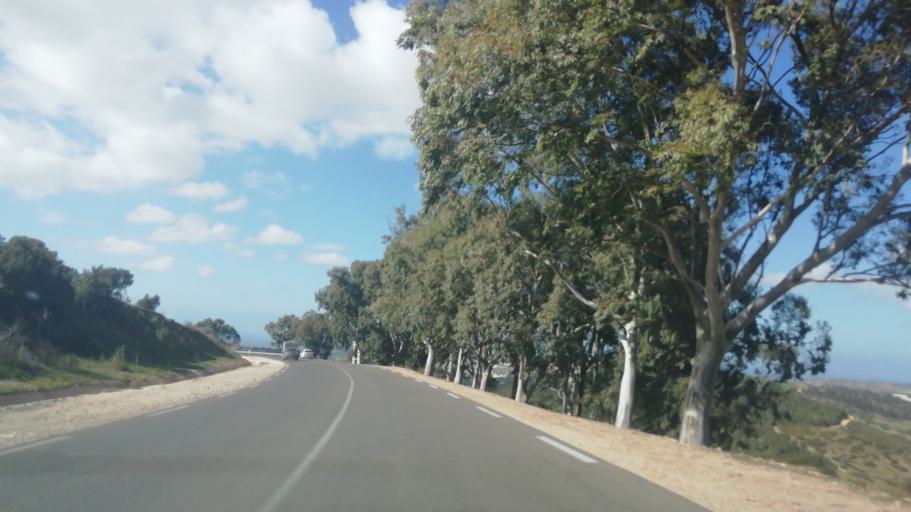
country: DZ
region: Relizane
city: Relizane
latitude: 36.0892
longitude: 0.4742
